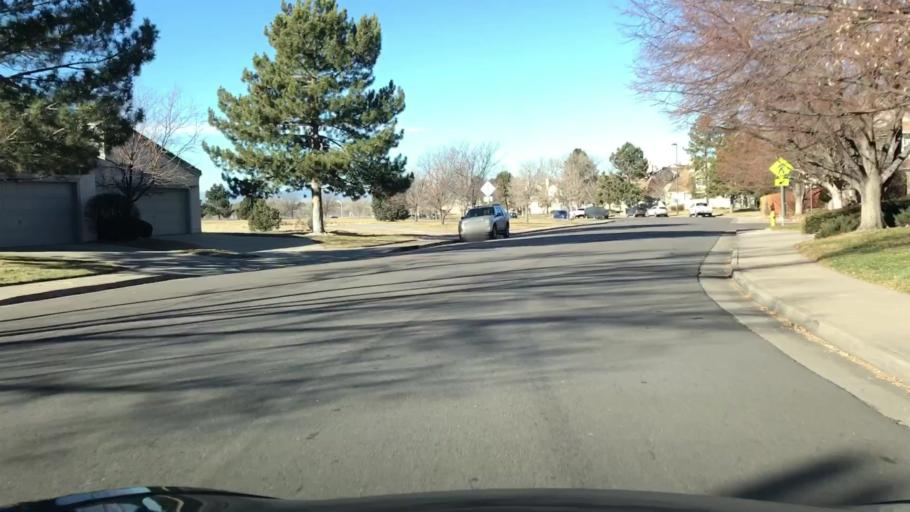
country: US
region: Colorado
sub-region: Arapahoe County
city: Glendale
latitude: 39.6869
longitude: -104.9003
